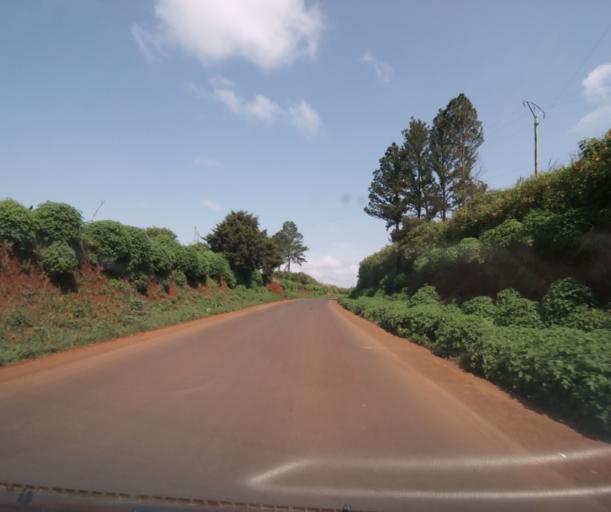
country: CM
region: West
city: Bansoa
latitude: 5.4954
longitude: 10.2568
